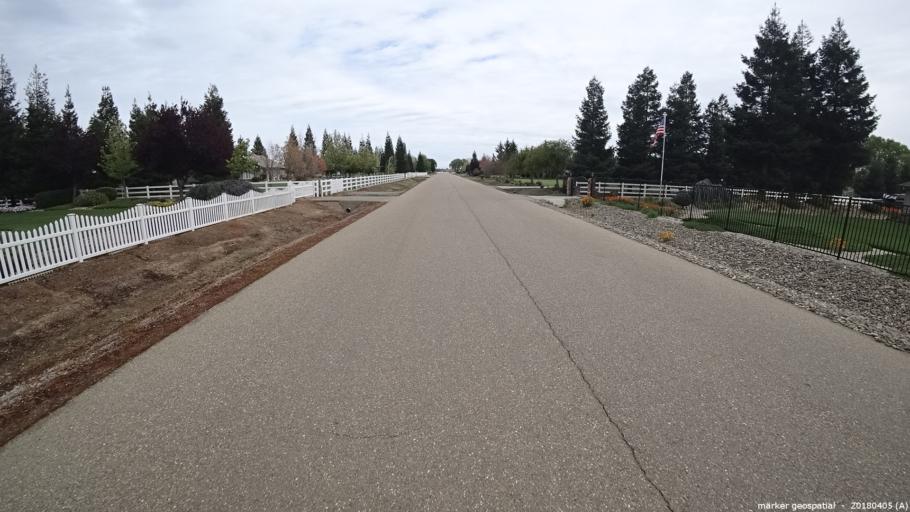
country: US
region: California
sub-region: Sacramento County
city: Galt
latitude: 38.2756
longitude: -121.3350
